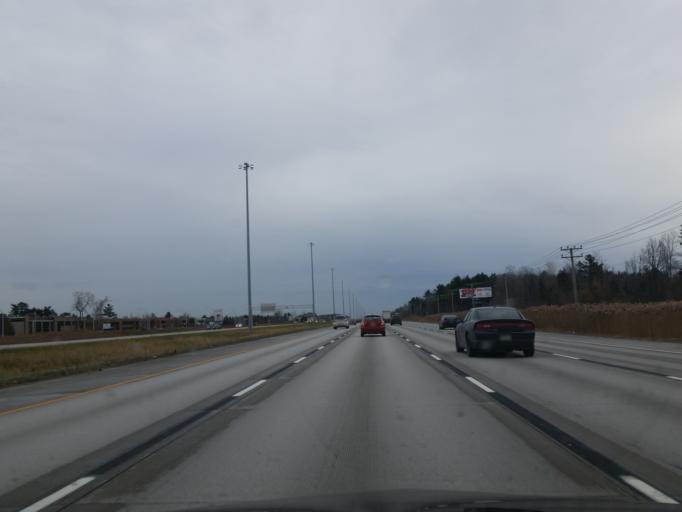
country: CA
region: Quebec
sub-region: Laurentides
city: Blainville
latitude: 45.6689
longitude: -73.9024
